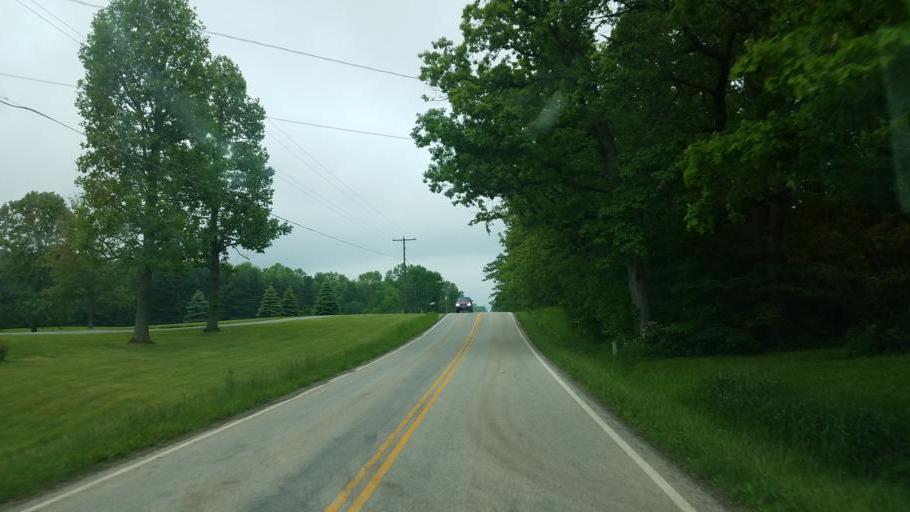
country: US
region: Ohio
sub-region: Ashland County
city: Ashland
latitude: 40.7938
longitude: -82.3397
